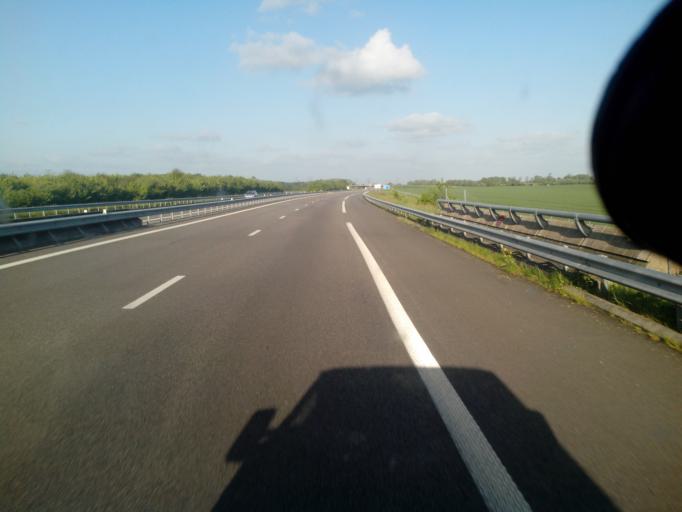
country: FR
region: Haute-Normandie
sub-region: Departement de la Seine-Maritime
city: Totes
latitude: 49.6391
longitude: 1.0629
